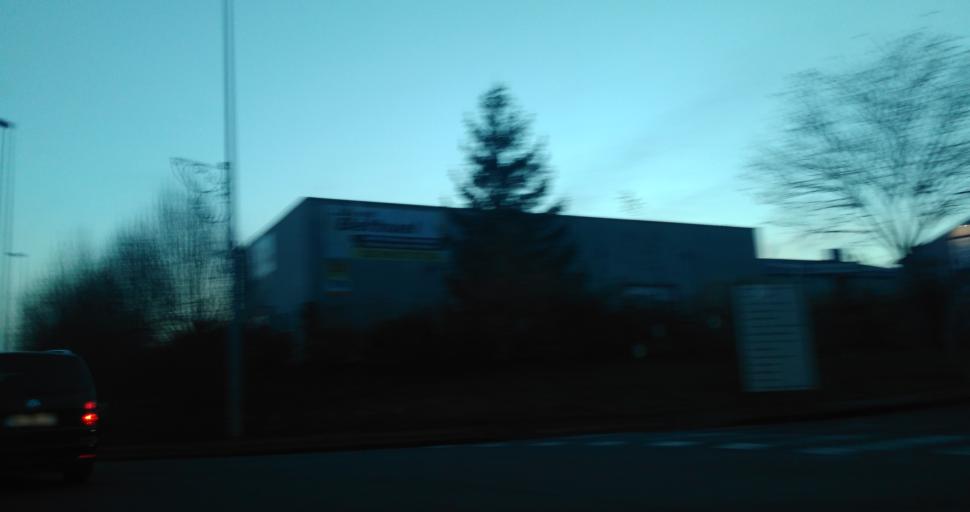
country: FR
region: Brittany
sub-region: Departement d'Ille-et-Vilaine
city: Pleumeleuc
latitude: 48.1797
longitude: -1.9199
